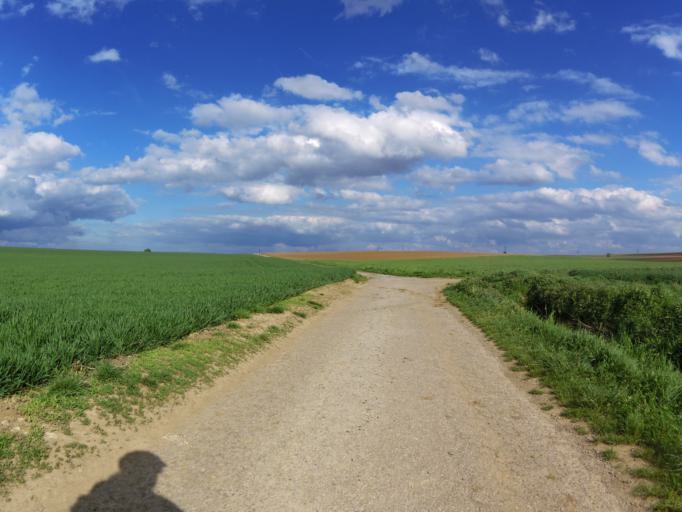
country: DE
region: Bavaria
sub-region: Regierungsbezirk Unterfranken
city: Oberpleichfeld
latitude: 49.8668
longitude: 10.0671
